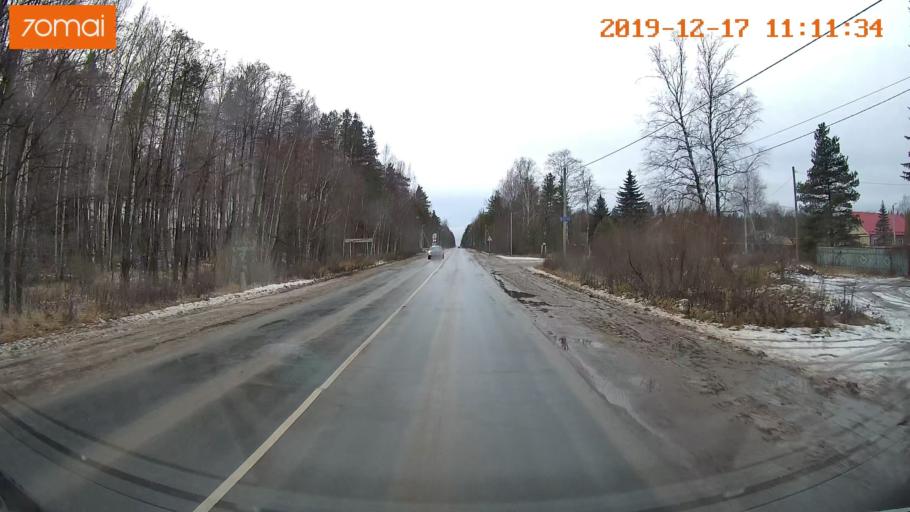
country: RU
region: Vladimir
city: Gus'-Khrustal'nyy
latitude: 55.5855
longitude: 40.6359
